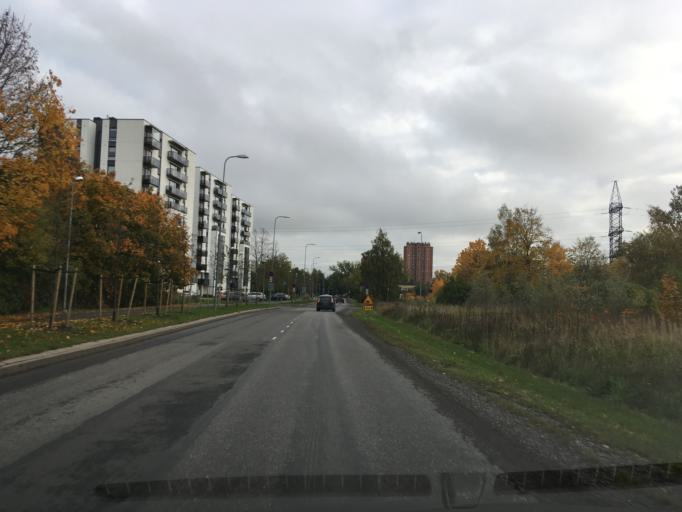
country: EE
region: Harju
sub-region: Tallinna linn
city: Kose
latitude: 59.4451
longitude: 24.8268
